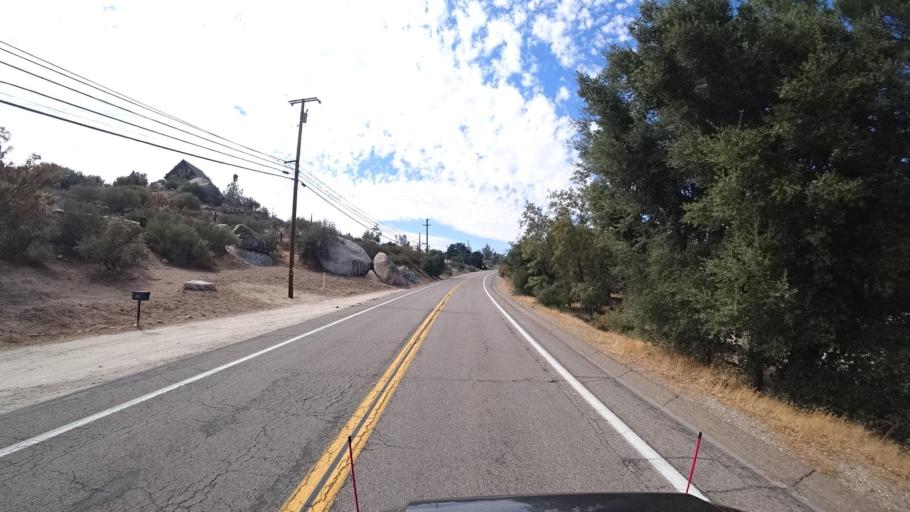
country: MX
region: Baja California
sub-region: Tecate
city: Cereso del Hongo
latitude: 32.6660
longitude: -116.2828
